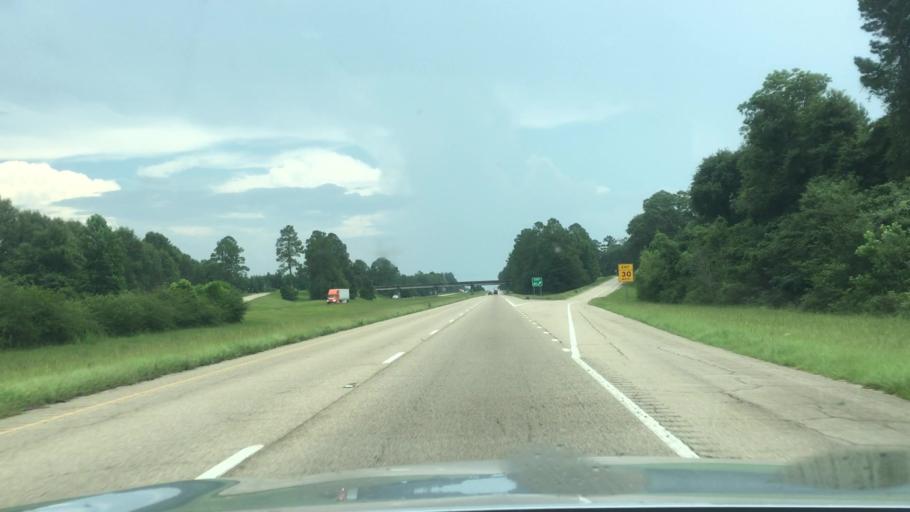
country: US
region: Mississippi
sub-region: Lamar County
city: Lumberton
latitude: 30.9970
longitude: -89.4203
